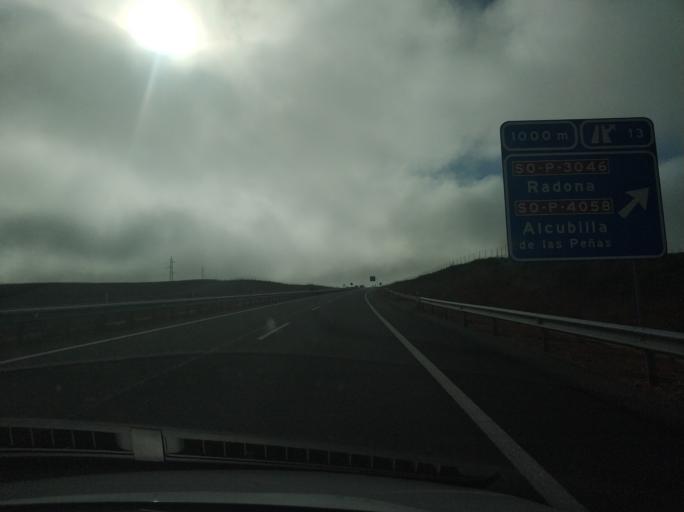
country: ES
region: Castille and Leon
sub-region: Provincia de Soria
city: Alcubilla de las Penas
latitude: 41.2760
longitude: -2.4749
